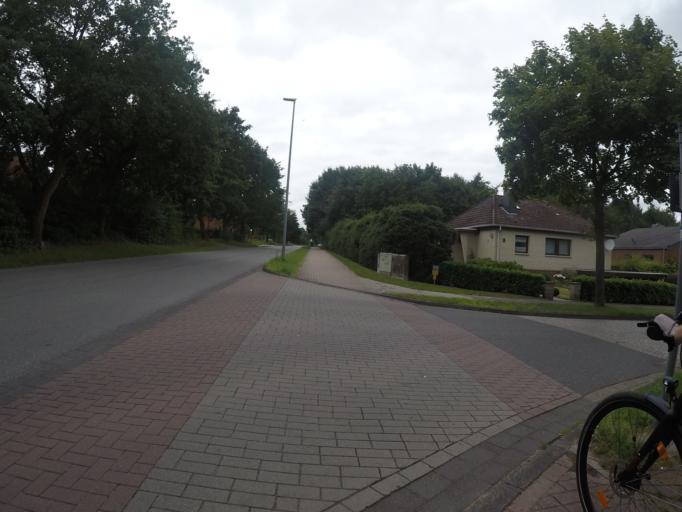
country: DE
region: Lower Saxony
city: Hammah
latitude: 53.5997
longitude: 9.4111
